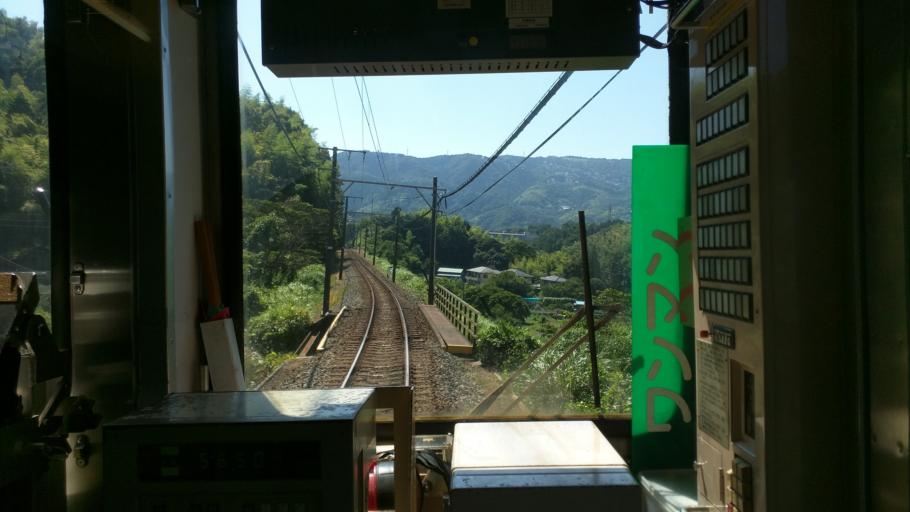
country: JP
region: Shizuoka
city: Ito
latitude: 34.9507
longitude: 139.1034
